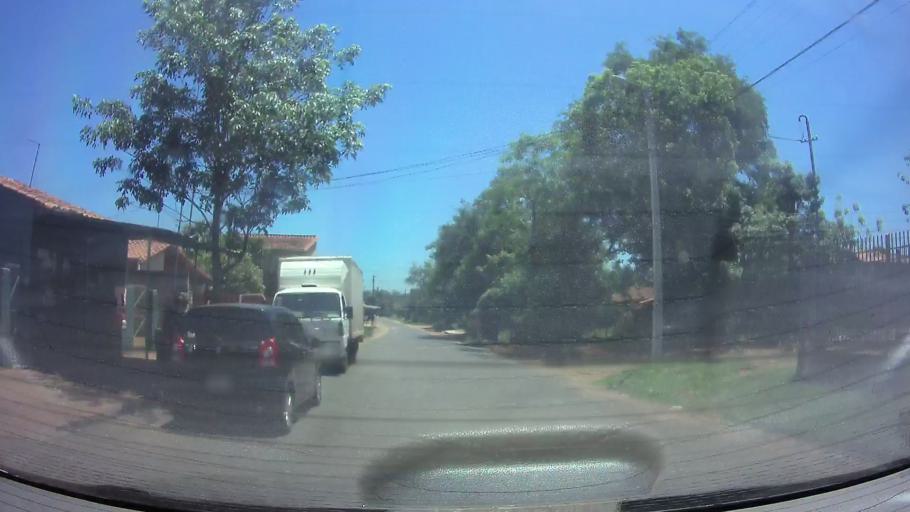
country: PY
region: Central
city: San Lorenzo
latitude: -25.3508
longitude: -57.4897
